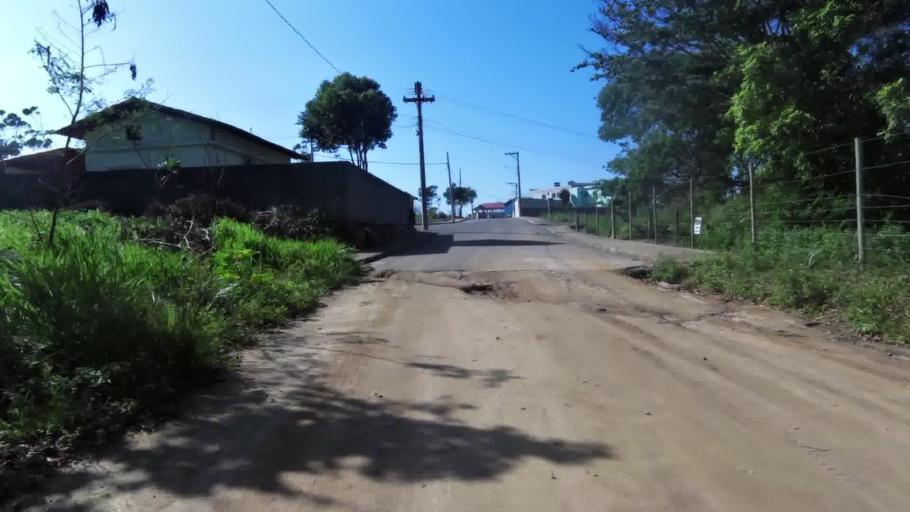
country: BR
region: Espirito Santo
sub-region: Piuma
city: Piuma
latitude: -20.8187
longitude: -40.6252
